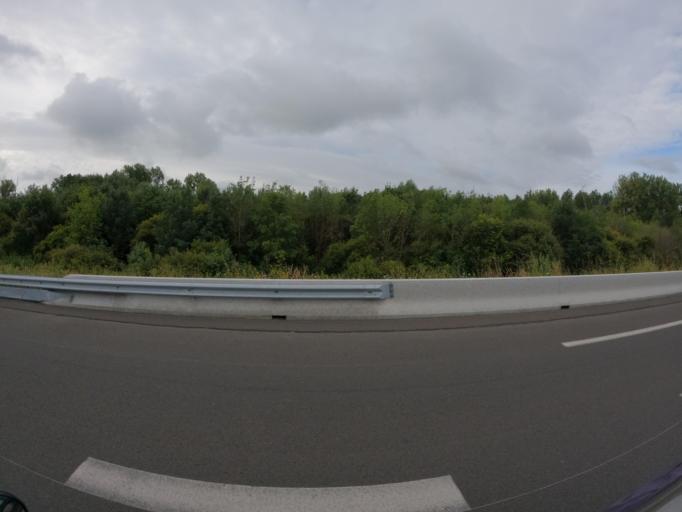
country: FR
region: Centre
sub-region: Departement d'Indre-et-Loire
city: Cinq-Mars-la-Pile
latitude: 47.3341
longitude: 0.4430
